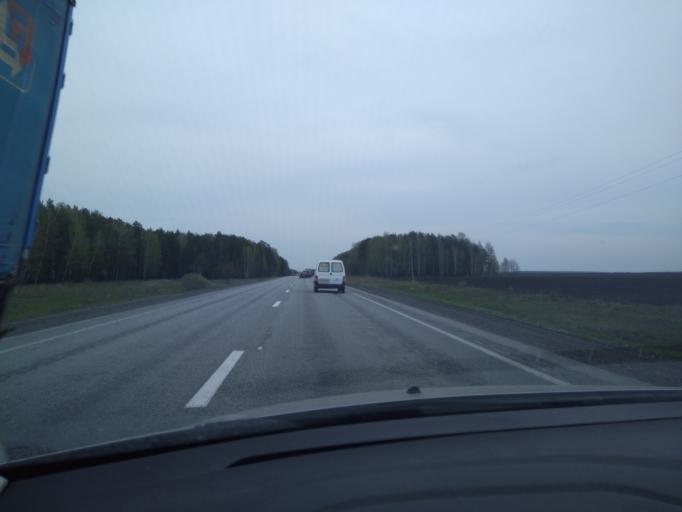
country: RU
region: Sverdlovsk
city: Gryaznovskoye
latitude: 56.7819
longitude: 61.6238
